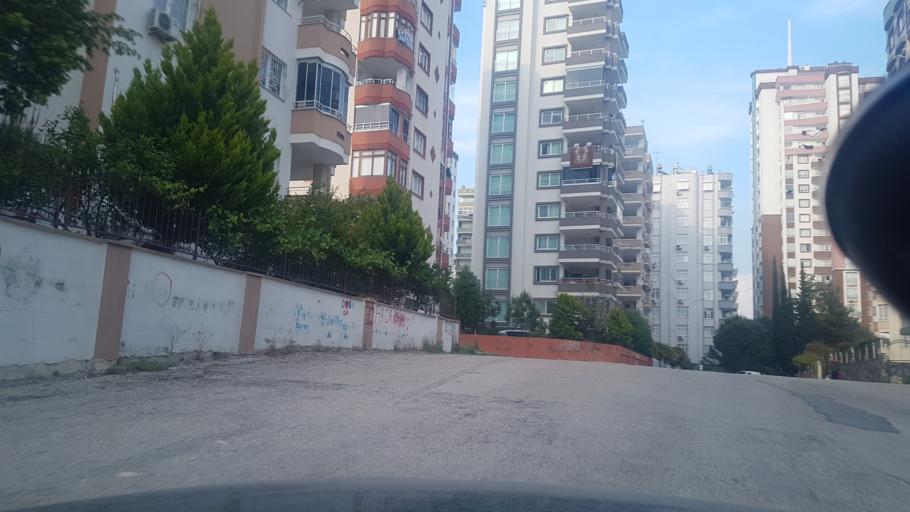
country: TR
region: Adana
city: Seyhan
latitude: 37.0470
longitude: 35.2742
